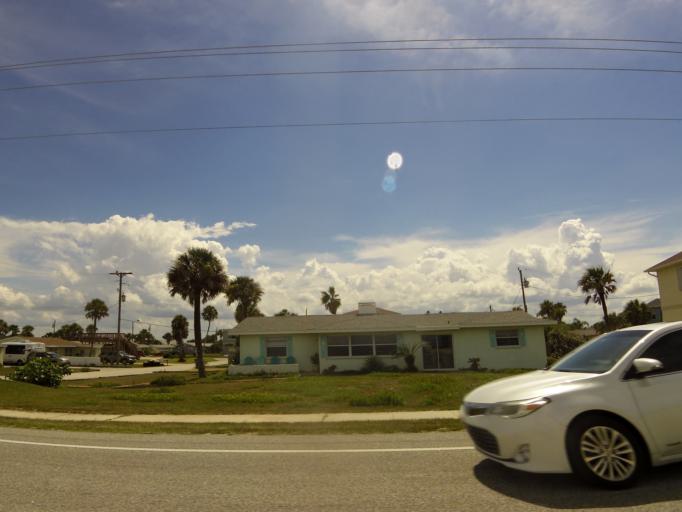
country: US
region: Florida
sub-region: Volusia County
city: Ormond-by-the-Sea
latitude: 29.3842
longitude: -81.0830
